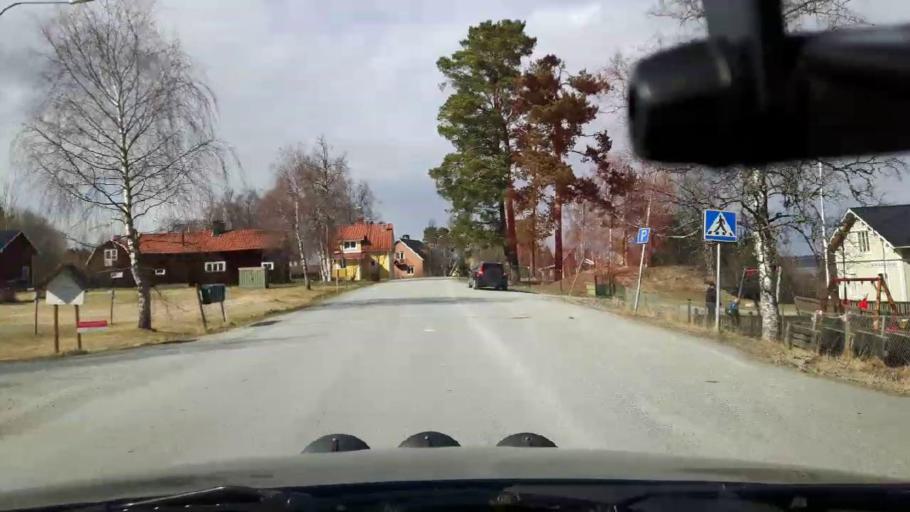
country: SE
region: Jaemtland
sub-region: Bergs Kommun
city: Hoverberg
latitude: 62.9137
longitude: 14.3367
